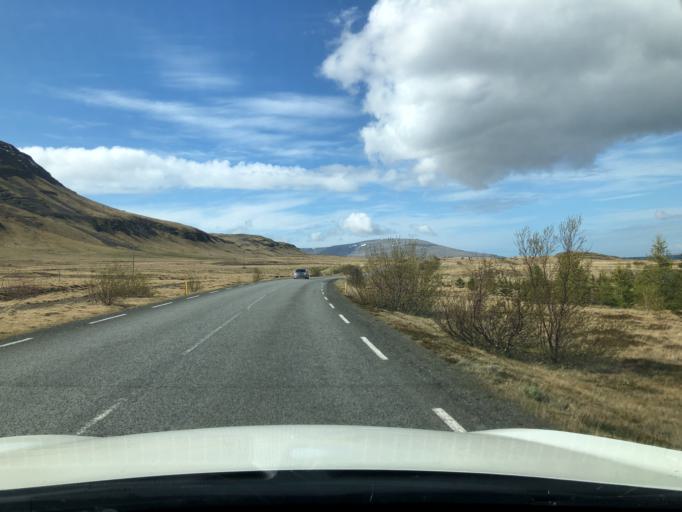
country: IS
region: Capital Region
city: Mosfellsbaer
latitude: 64.3299
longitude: -21.6680
